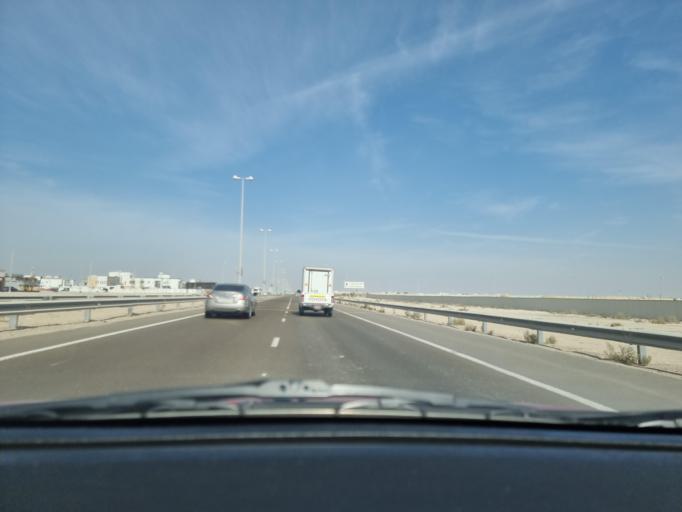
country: AE
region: Abu Dhabi
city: Abu Dhabi
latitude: 24.3732
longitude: 54.6737
